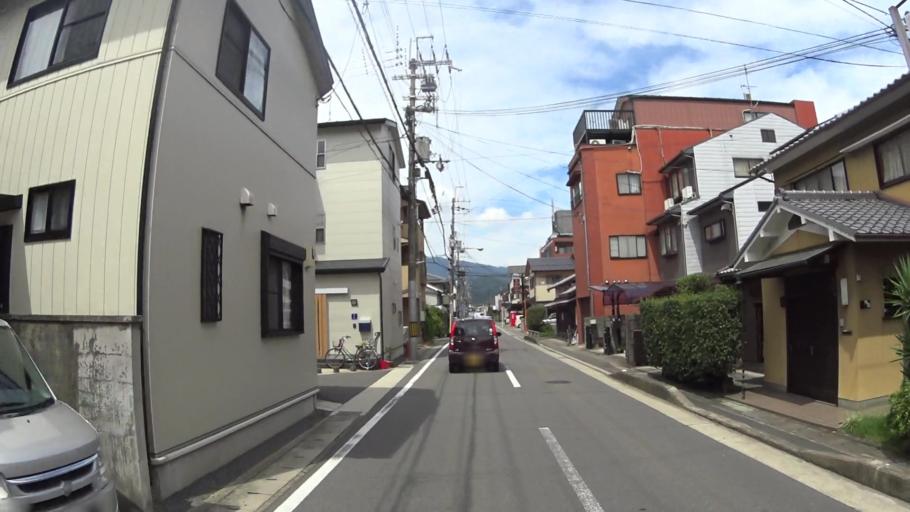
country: JP
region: Kyoto
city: Muko
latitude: 35.0077
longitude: 135.6821
